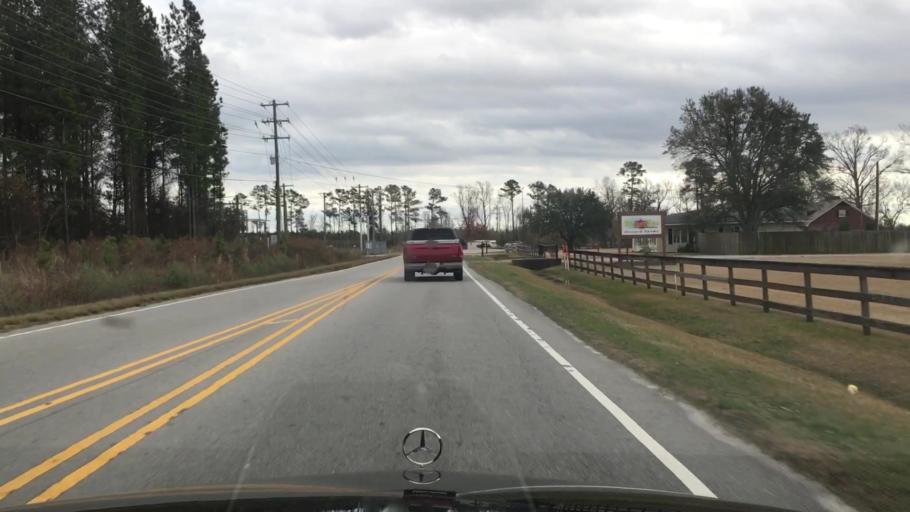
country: US
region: North Carolina
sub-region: Onslow County
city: Half Moon
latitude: 34.8526
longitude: -77.4836
